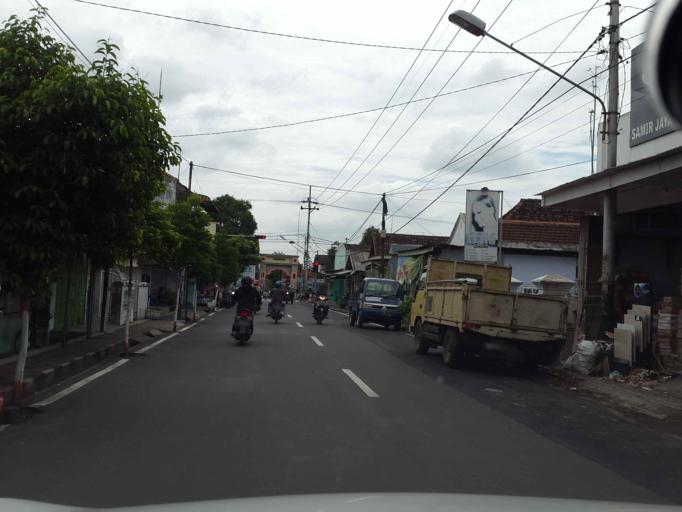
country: ID
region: East Java
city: Soko
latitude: -7.4790
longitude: 112.4277
